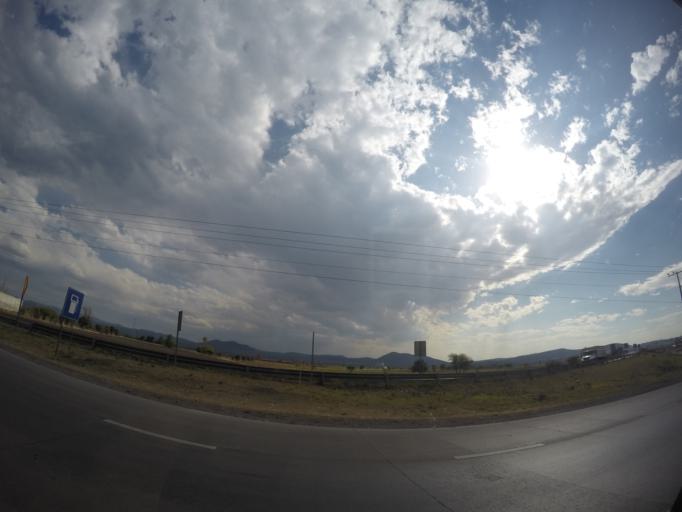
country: MX
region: Queretaro
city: El Sauz
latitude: 20.4915
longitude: -100.1259
